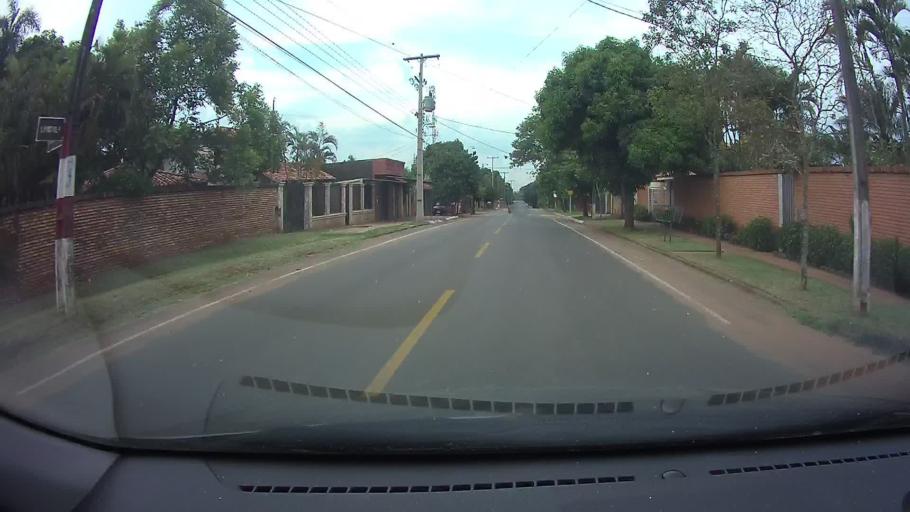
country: PY
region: Central
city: San Lorenzo
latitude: -25.2735
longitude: -57.4774
